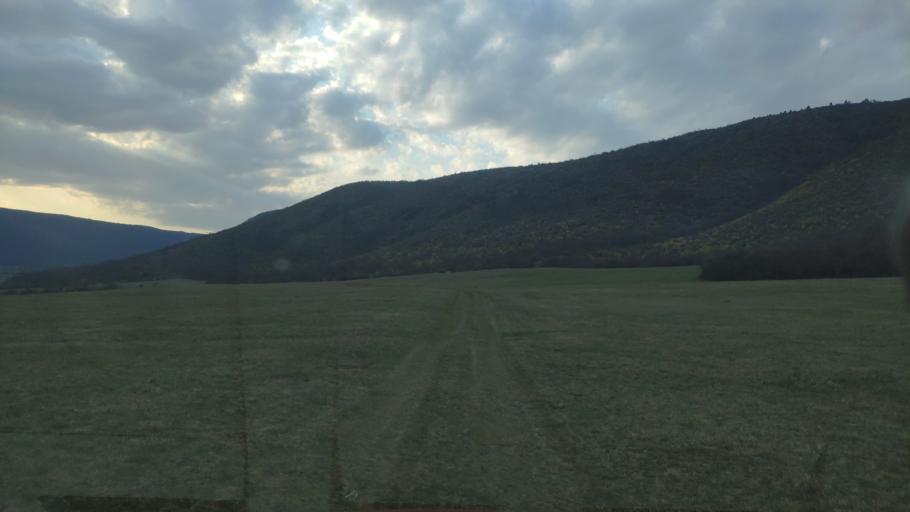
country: SK
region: Kosicky
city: Medzev
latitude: 48.6227
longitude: 20.9041
